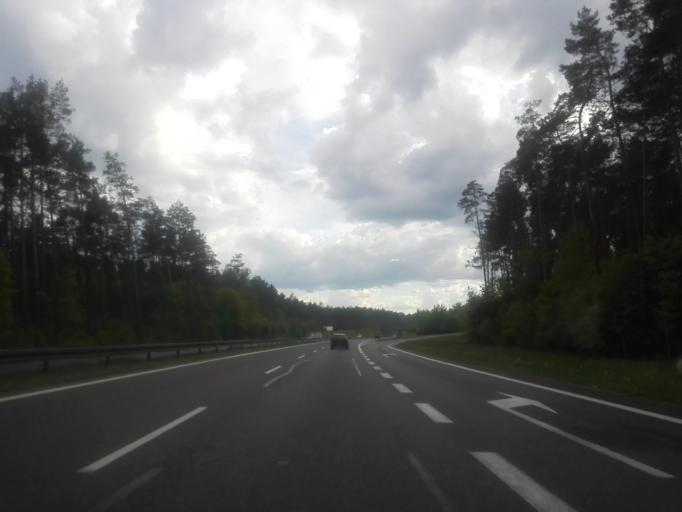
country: PL
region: Masovian Voivodeship
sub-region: Powiat ostrowski
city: Ostrow Mazowiecka
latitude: 52.7878
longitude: 21.8639
